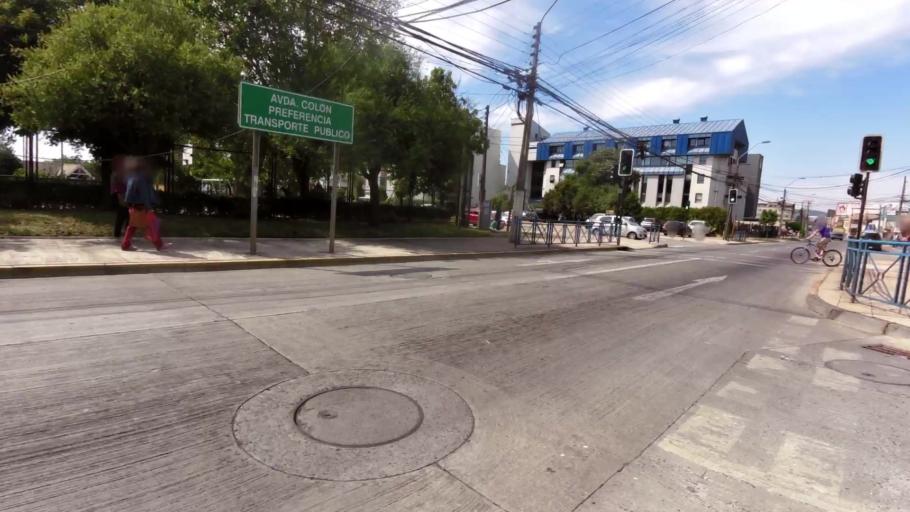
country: CL
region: Biobio
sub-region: Provincia de Concepcion
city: Talcahuano
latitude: -36.7194
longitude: -73.1102
